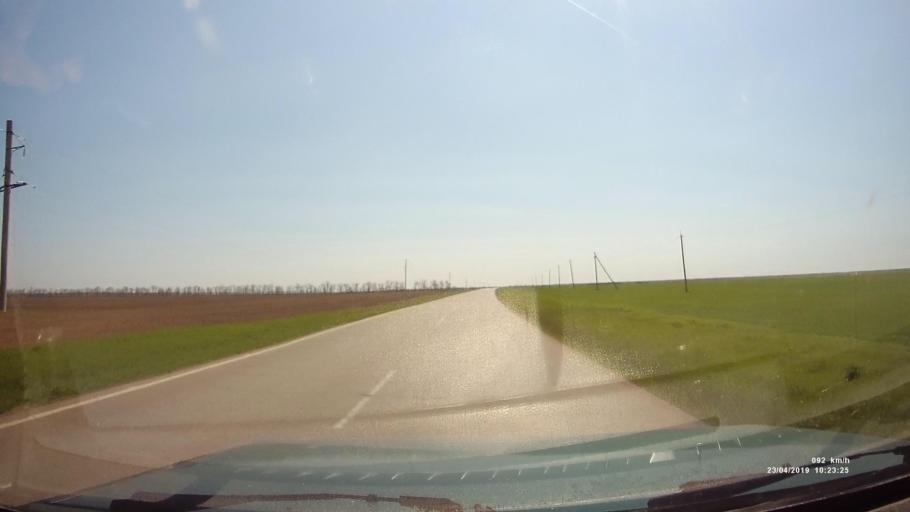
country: RU
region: Rostov
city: Sovetskoye
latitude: 46.6476
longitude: 42.4242
